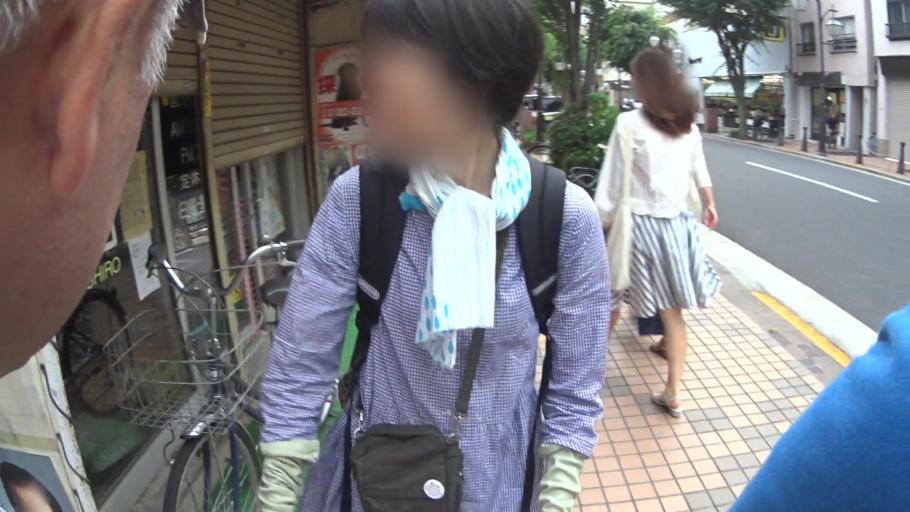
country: JP
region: Tokyo
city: Urayasu
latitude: 35.7081
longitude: 139.8430
